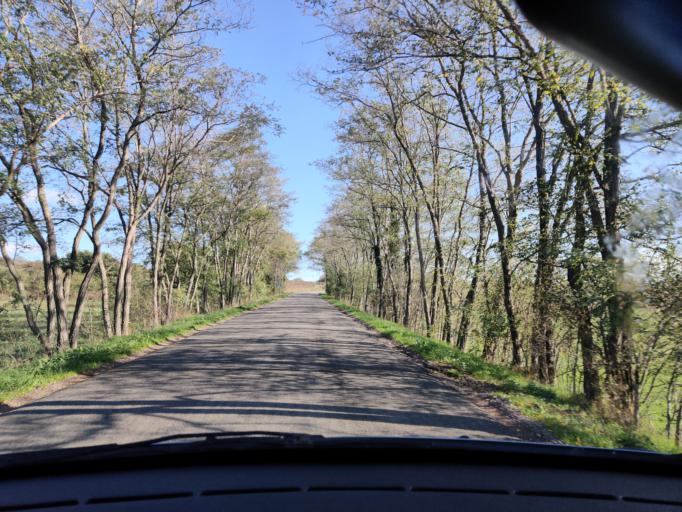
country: FR
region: Auvergne
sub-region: Departement du Puy-de-Dome
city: Combronde
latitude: 46.0277
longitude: 3.1064
